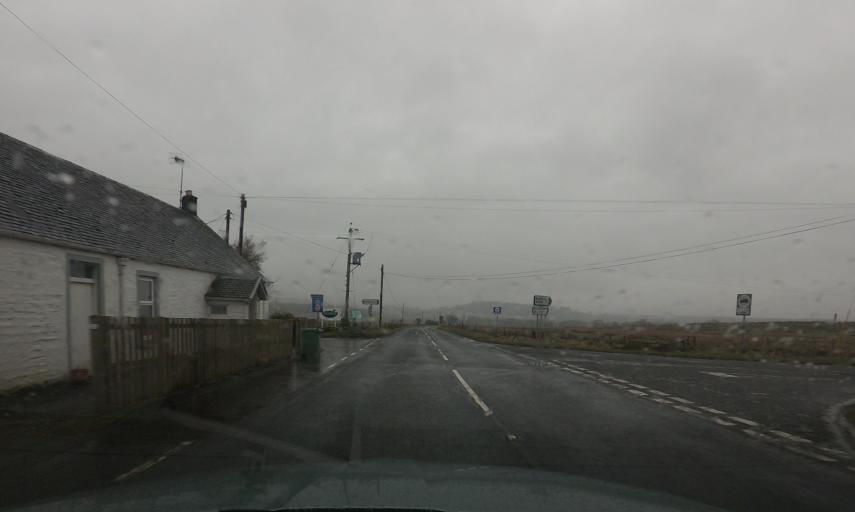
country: GB
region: Scotland
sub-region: Stirling
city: Balfron
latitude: 56.1202
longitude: -4.3594
